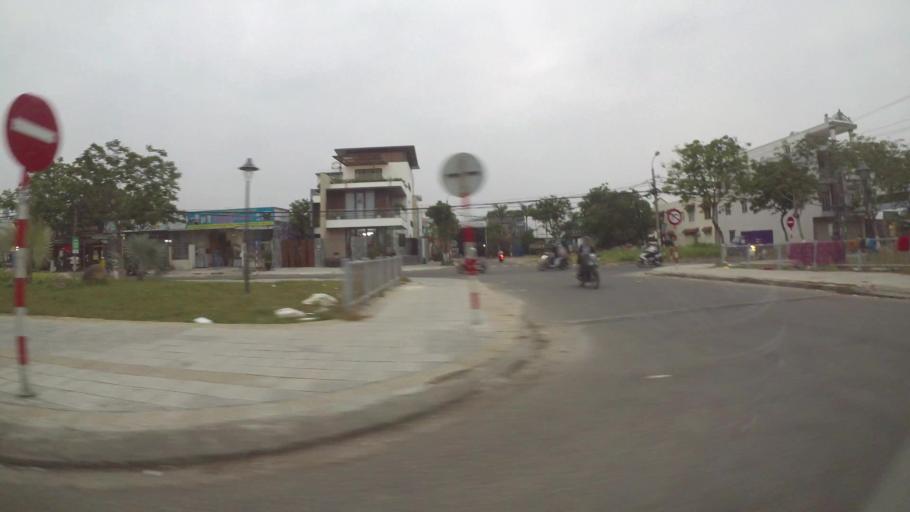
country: VN
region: Da Nang
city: Thanh Khe
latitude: 16.0545
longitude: 108.1773
